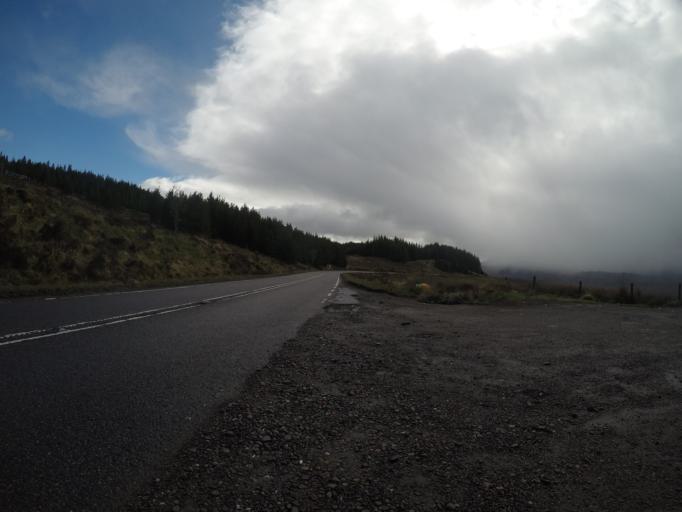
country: GB
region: Scotland
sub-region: Highland
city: Spean Bridge
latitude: 57.0867
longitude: -4.9642
